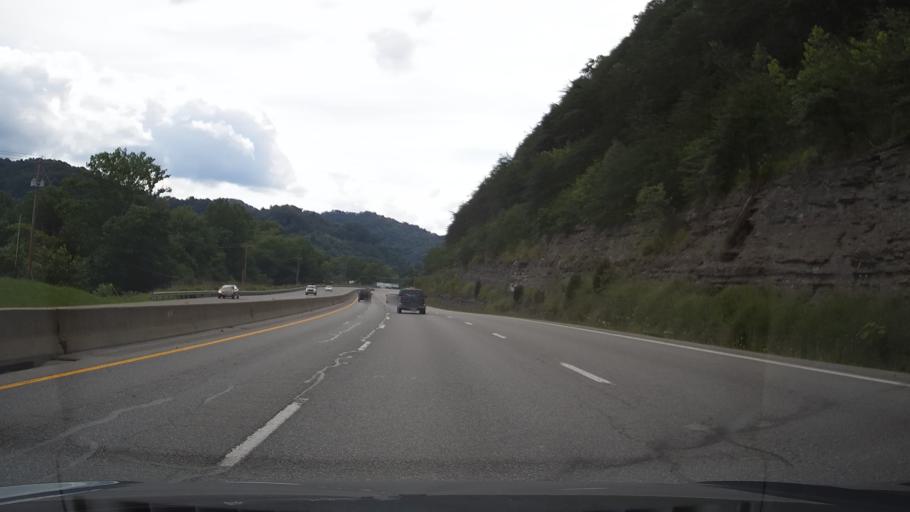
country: US
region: Kentucky
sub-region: Pike County
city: Coal Run Village
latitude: 37.5105
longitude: -82.5424
